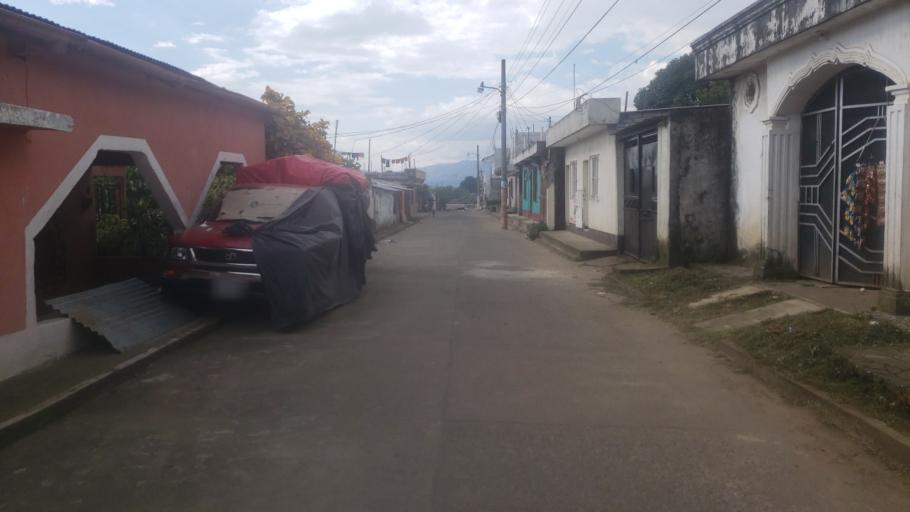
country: GT
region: Suchitepeque
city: Pueblo Nuevo
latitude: 14.6489
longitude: -91.5542
